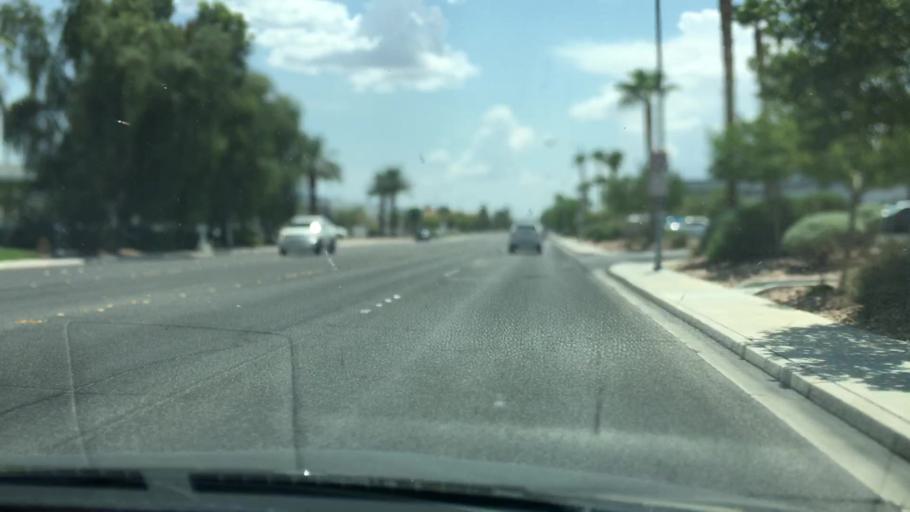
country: US
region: Nevada
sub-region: Clark County
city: Whitney
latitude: 36.0763
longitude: -115.0917
